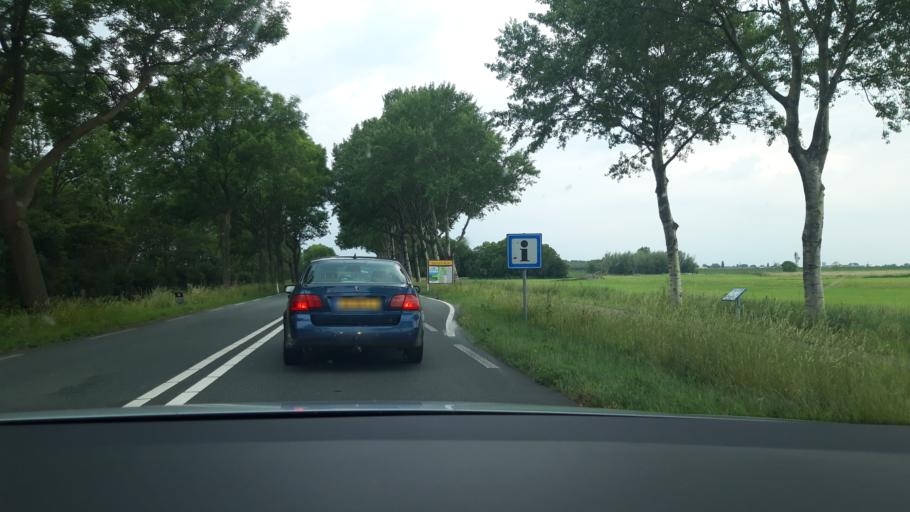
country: NL
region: North Holland
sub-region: Gemeente Zaanstad
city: Zaanstad
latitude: 52.4759
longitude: 4.8492
